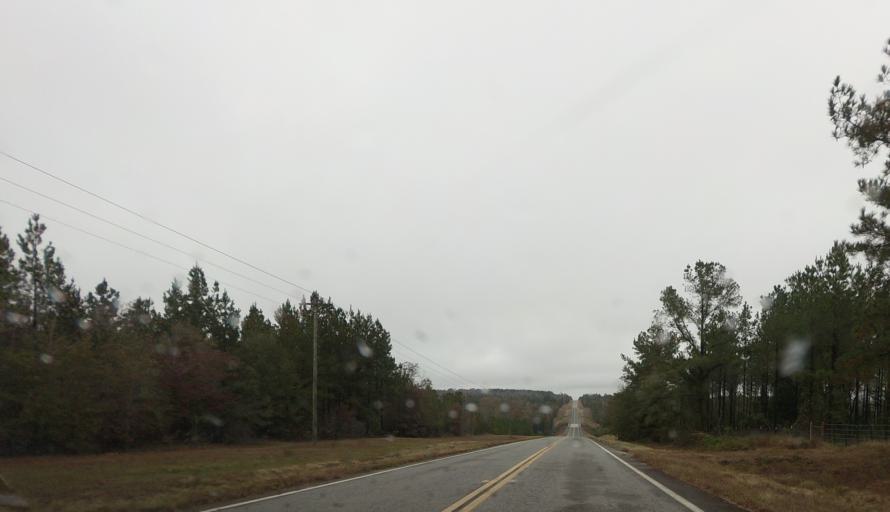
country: US
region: Georgia
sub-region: Marion County
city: Buena Vista
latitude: 32.4250
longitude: -84.3850
